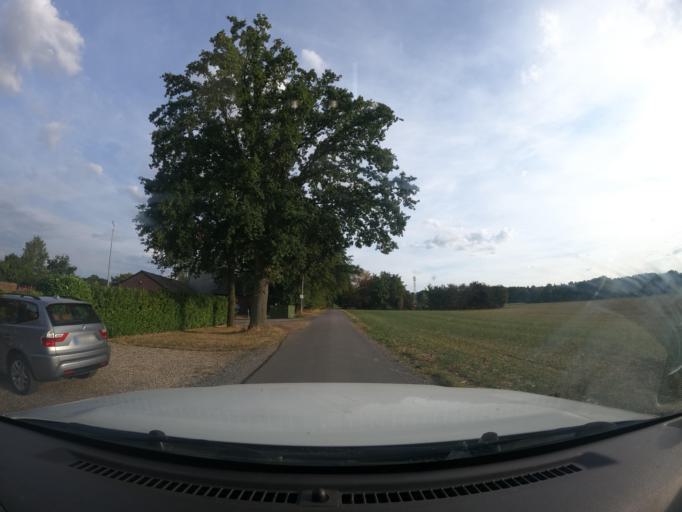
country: DE
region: North Rhine-Westphalia
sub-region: Regierungsbezirk Dusseldorf
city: Hamminkeln
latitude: 51.7004
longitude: 6.5930
